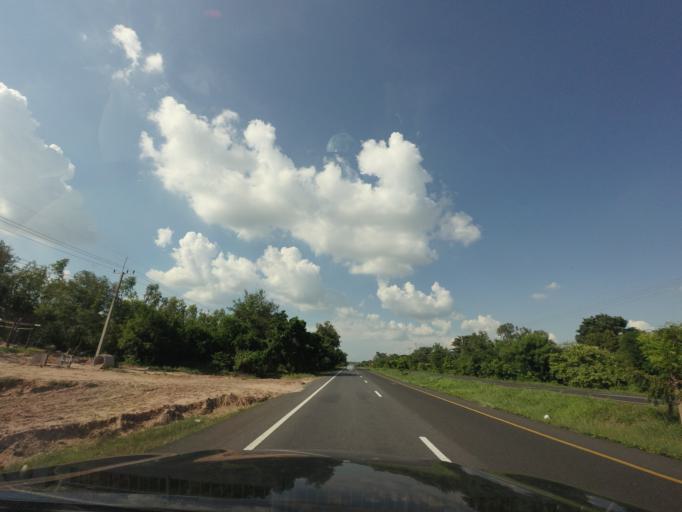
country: TH
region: Nakhon Ratchasima
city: Bua Lai
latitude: 15.6734
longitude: 102.5757
